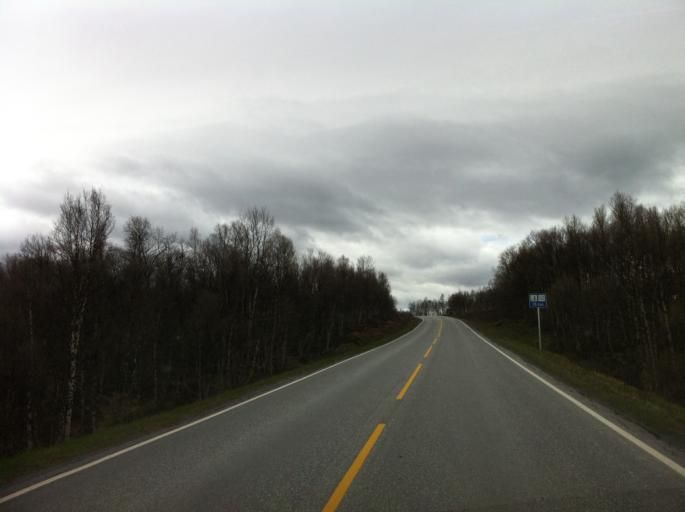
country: NO
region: Sor-Trondelag
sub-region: Tydal
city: Aas
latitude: 62.6436
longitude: 11.8455
